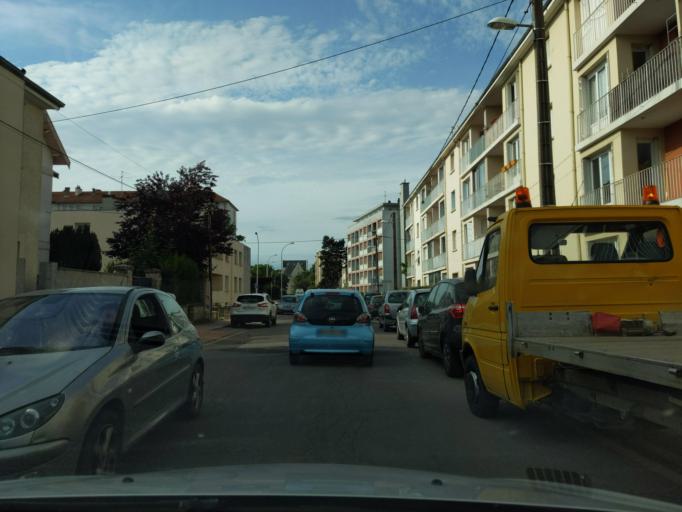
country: FR
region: Bourgogne
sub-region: Departement de la Cote-d'Or
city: Saint-Apollinaire
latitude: 47.3276
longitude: 5.0596
